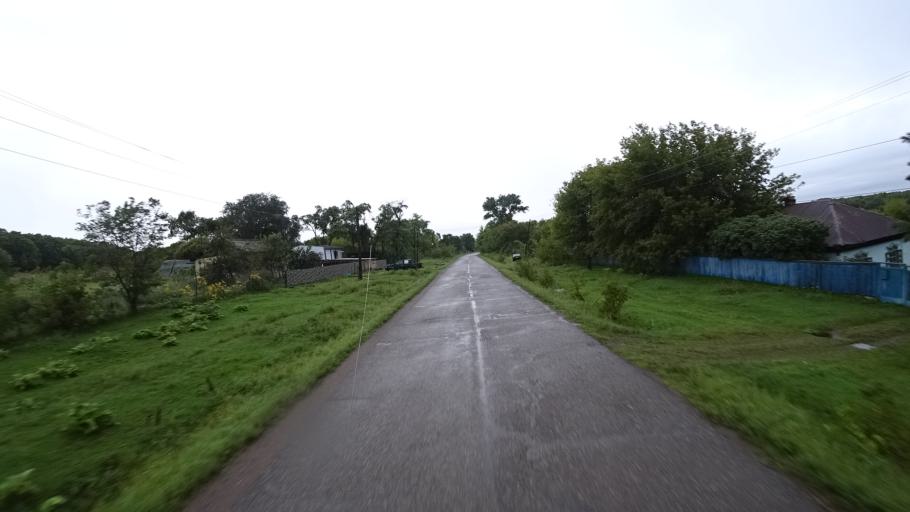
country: RU
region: Primorskiy
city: Monastyrishche
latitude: 44.2665
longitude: 132.4204
